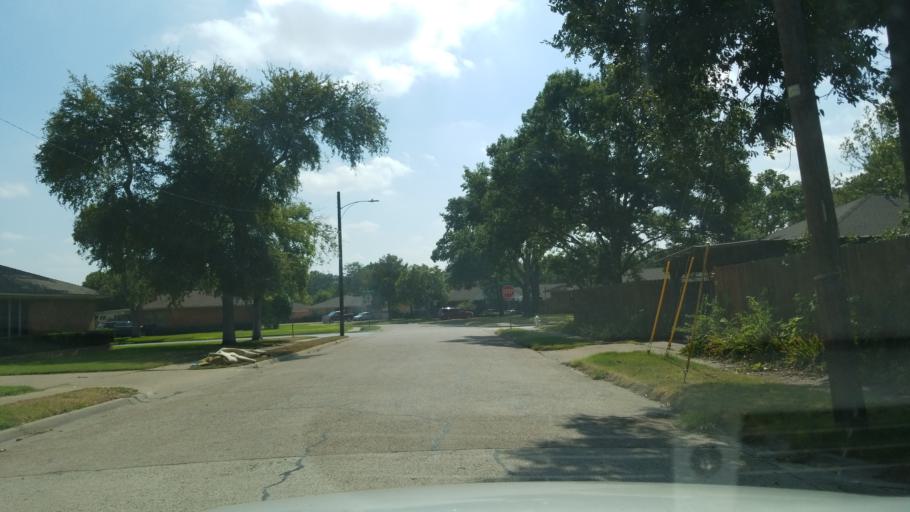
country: US
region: Texas
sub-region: Dallas County
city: Garland
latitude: 32.8992
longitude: -96.6635
